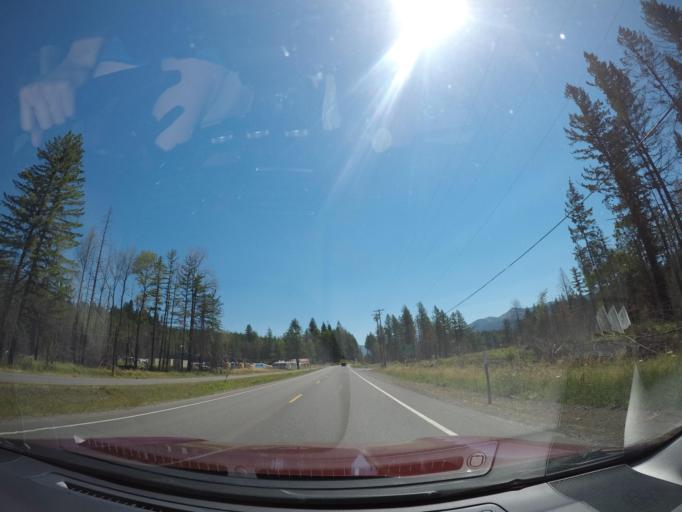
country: US
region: Oregon
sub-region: Linn County
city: Mill City
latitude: 44.7570
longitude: -122.4375
